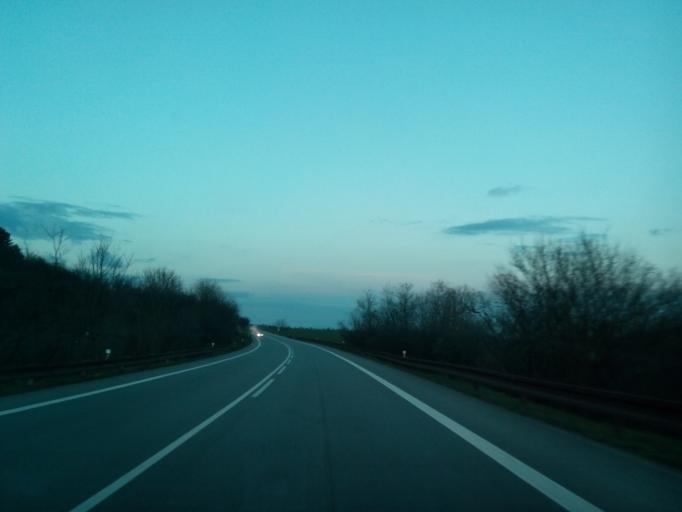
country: SK
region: Kosicky
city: Medzev
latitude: 48.5997
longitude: 20.8101
